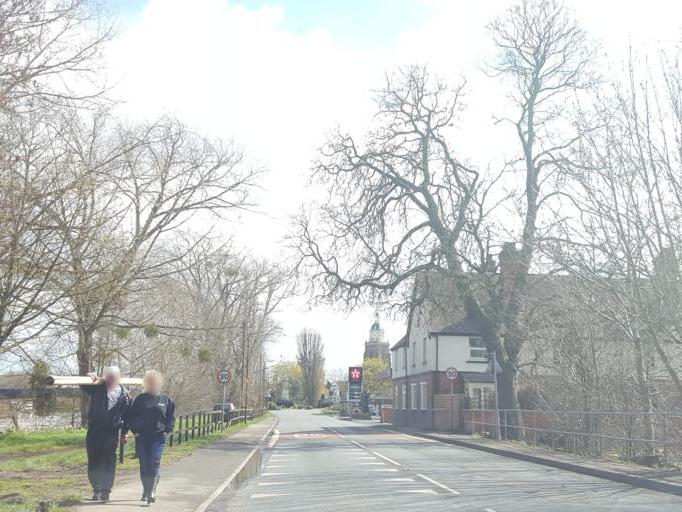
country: GB
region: England
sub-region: Worcestershire
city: Upton upon Severn
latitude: 52.0662
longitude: -2.2216
